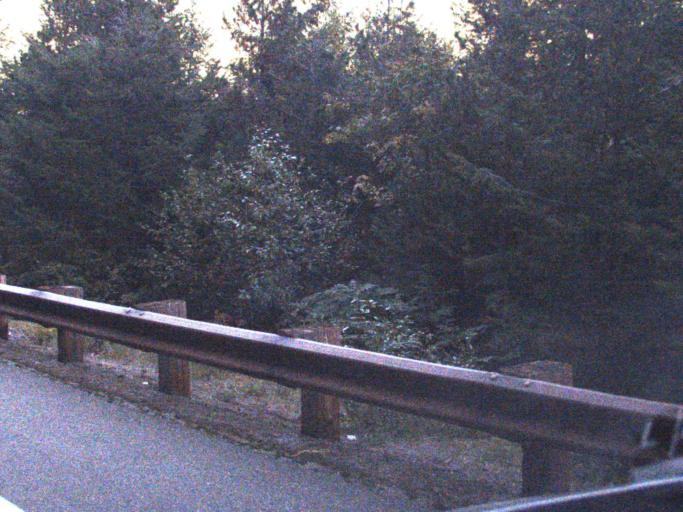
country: US
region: Washington
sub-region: Snohomish County
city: Darrington
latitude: 48.6533
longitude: -120.8587
